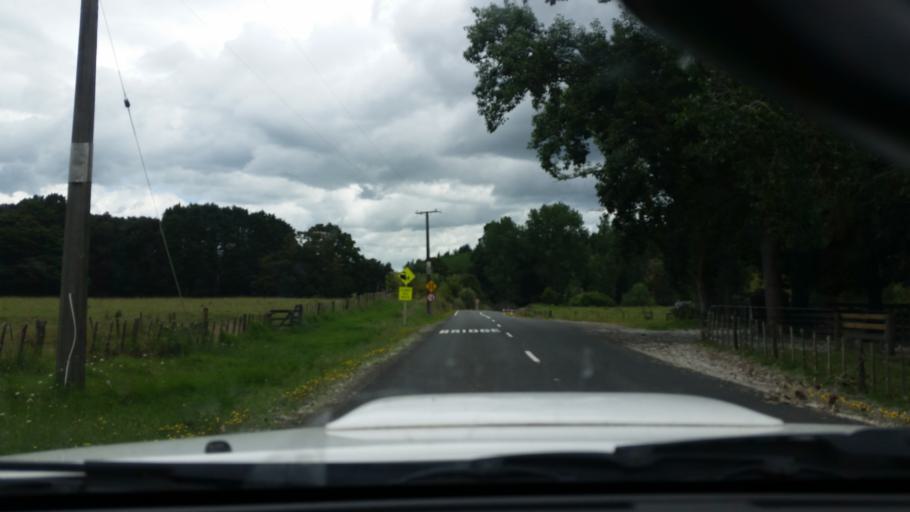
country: NZ
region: Northland
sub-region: Kaipara District
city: Dargaville
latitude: -35.7449
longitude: 173.8772
